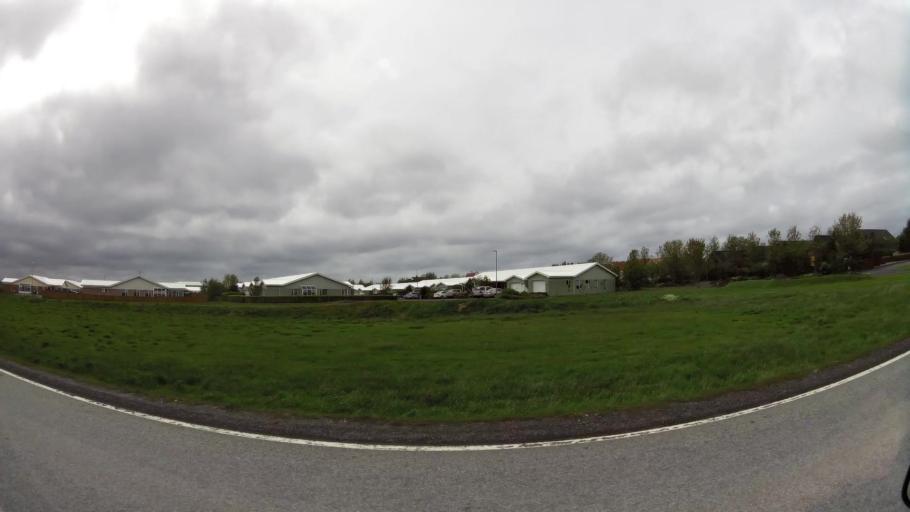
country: IS
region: Capital Region
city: Alftanes
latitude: 64.1059
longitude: -22.0097
